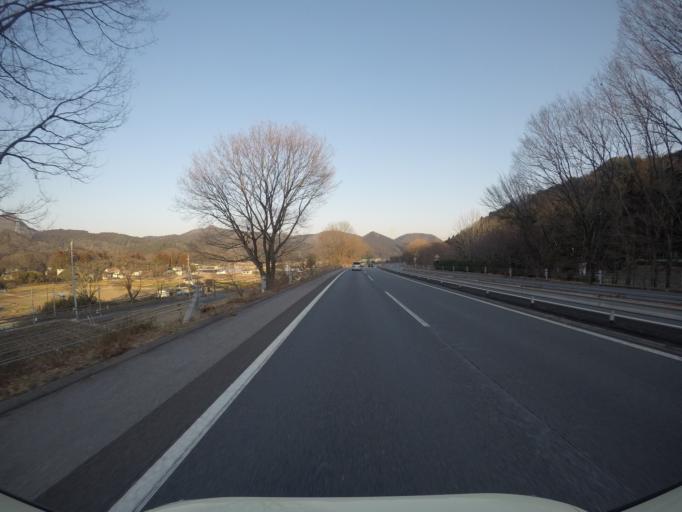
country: JP
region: Tochigi
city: Utsunomiya-shi
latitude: 36.6669
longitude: 139.8279
